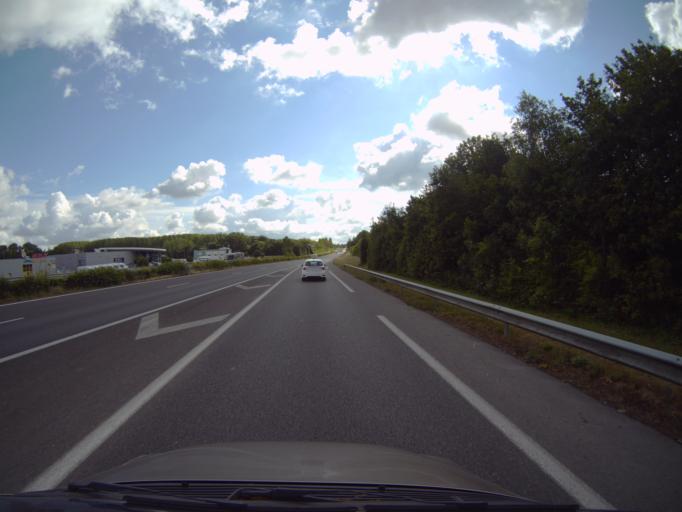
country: FR
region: Pays de la Loire
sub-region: Departement de la Vendee
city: Challans
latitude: 46.8557
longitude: -1.8934
